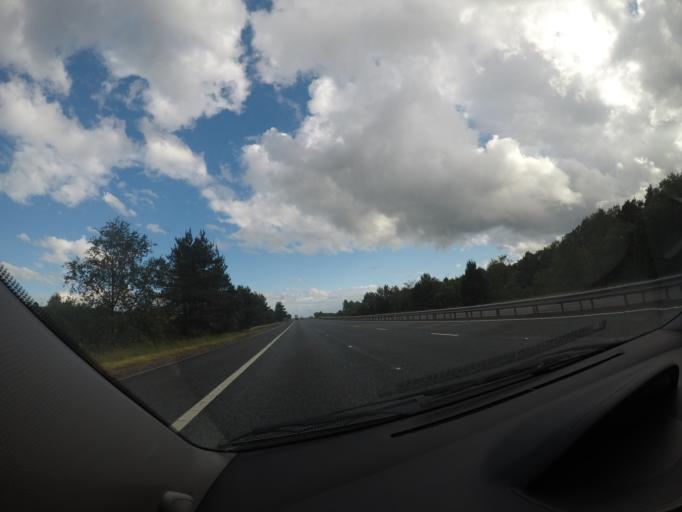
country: GB
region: Scotland
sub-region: Dumfries and Galloway
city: Lockerbie
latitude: 55.0885
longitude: -3.3190
